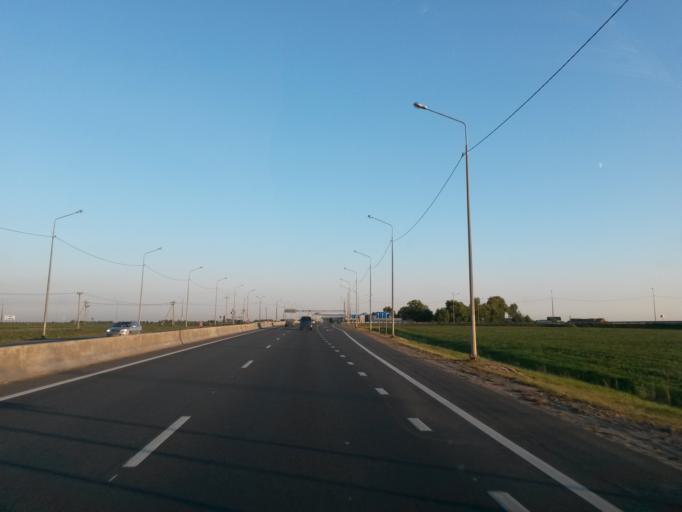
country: RU
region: Jaroslavl
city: Yaroslavl
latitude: 57.7232
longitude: 39.9009
